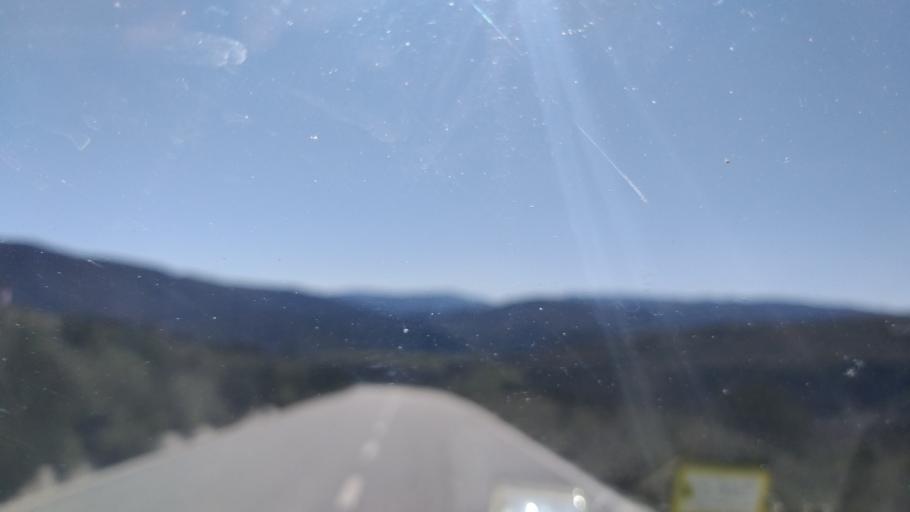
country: PT
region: Guarda
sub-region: Manteigas
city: Manteigas
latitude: 40.4675
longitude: -7.5029
